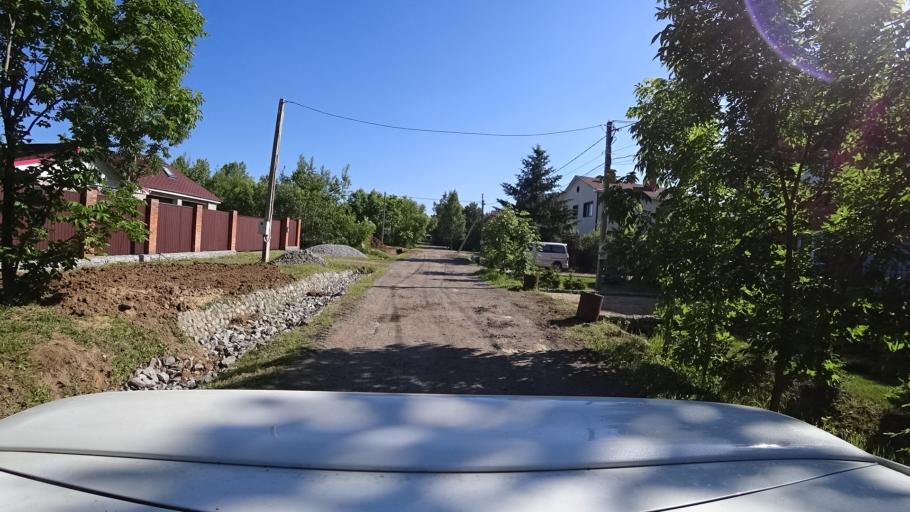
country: RU
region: Khabarovsk Krai
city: Topolevo
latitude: 48.5476
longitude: 135.1797
